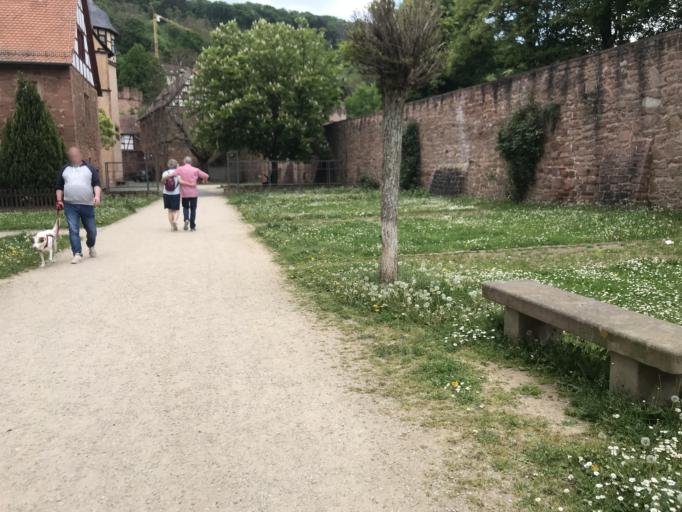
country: DE
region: Hesse
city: Budingen
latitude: 50.2931
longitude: 9.1174
